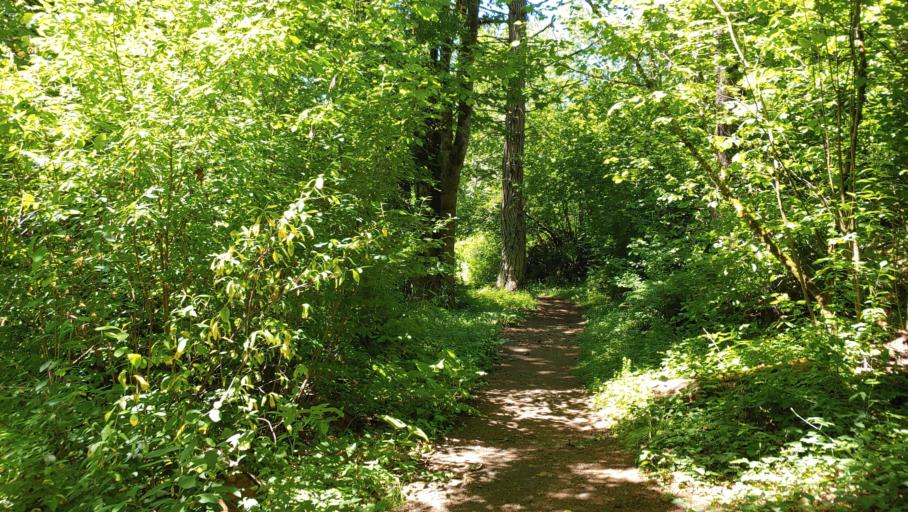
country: US
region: Washington
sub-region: King County
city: Newcastle
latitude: 47.5227
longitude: -122.1708
